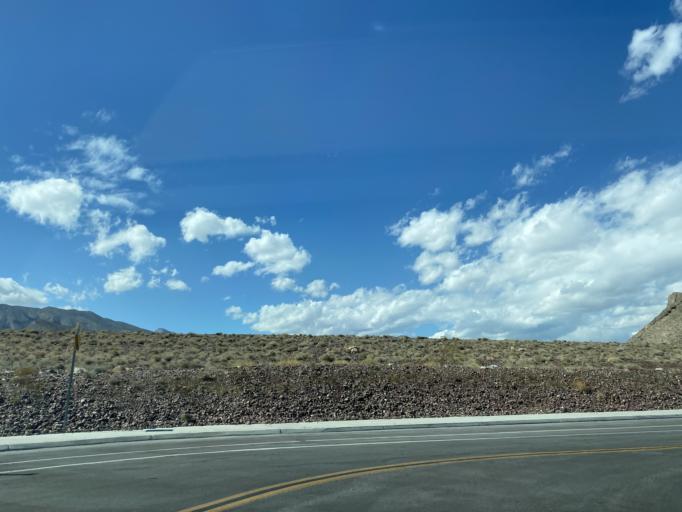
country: US
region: Nevada
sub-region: Clark County
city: Summerlin South
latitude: 36.2295
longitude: -115.3085
